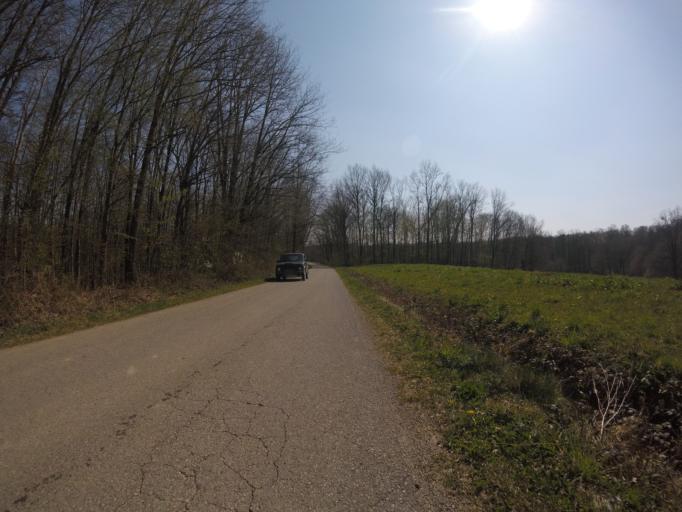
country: HR
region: Grad Zagreb
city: Strmec
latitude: 45.5641
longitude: 15.9204
